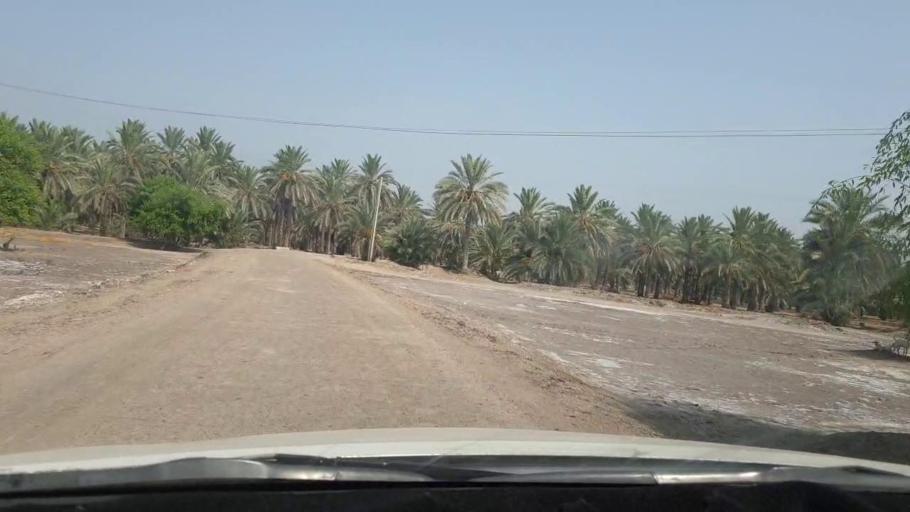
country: PK
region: Sindh
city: Rohri
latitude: 27.6259
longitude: 68.8877
